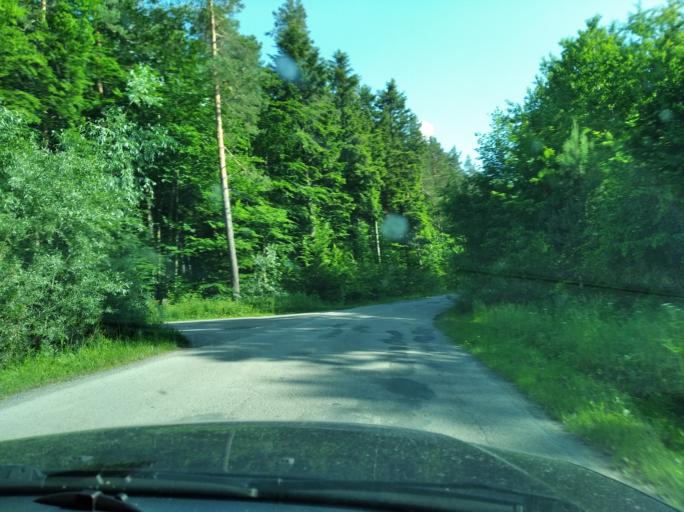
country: PL
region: Subcarpathian Voivodeship
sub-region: Powiat jaroslawski
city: Kramarzowka
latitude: 49.8526
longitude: 22.5169
